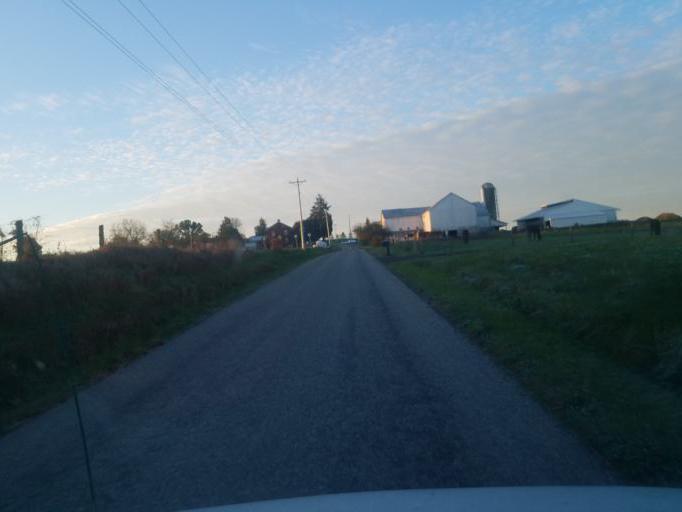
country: US
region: Ohio
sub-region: Stark County
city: Brewster
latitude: 40.6574
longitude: -81.7298
